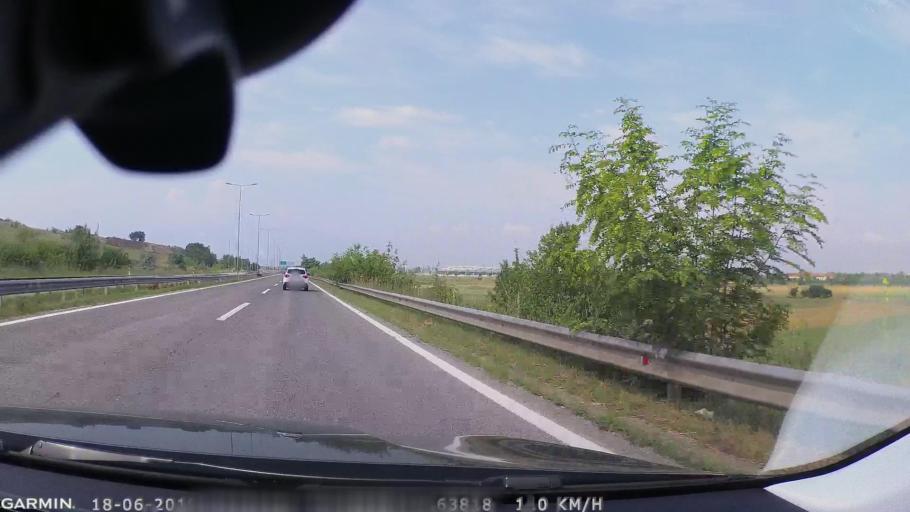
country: MK
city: Miladinovci
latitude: 41.9643
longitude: 21.6378
